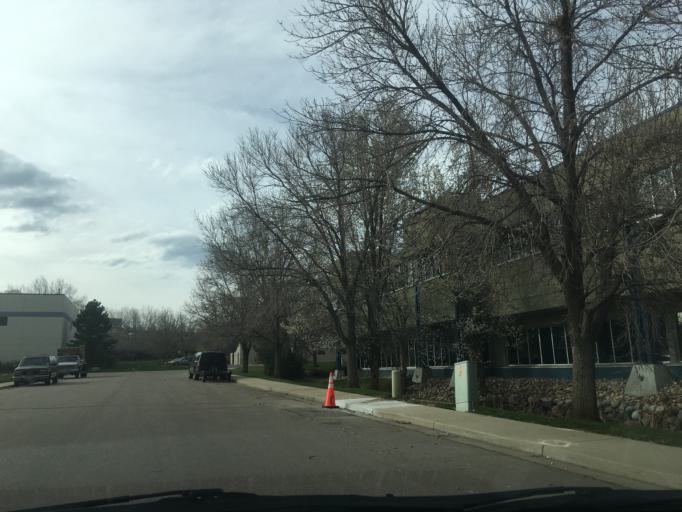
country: US
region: Colorado
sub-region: Boulder County
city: Boulder
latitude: 40.0315
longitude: -105.2269
